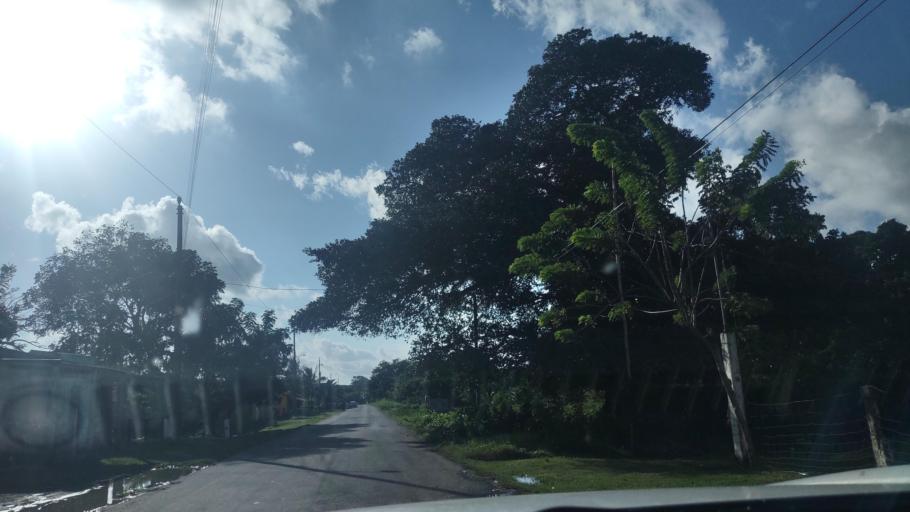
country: MX
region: Veracruz
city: El Tejar
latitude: 19.0704
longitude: -96.1689
